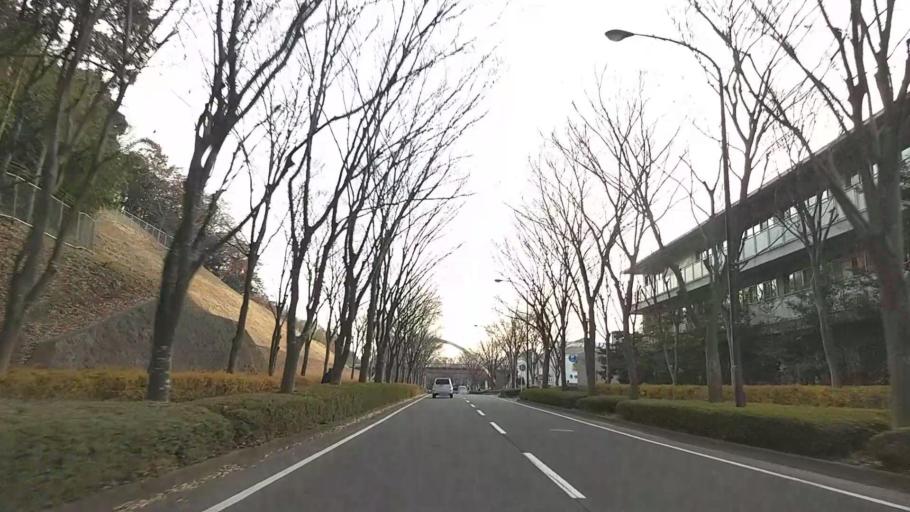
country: JP
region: Kanagawa
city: Atsugi
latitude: 35.4465
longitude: 139.3109
